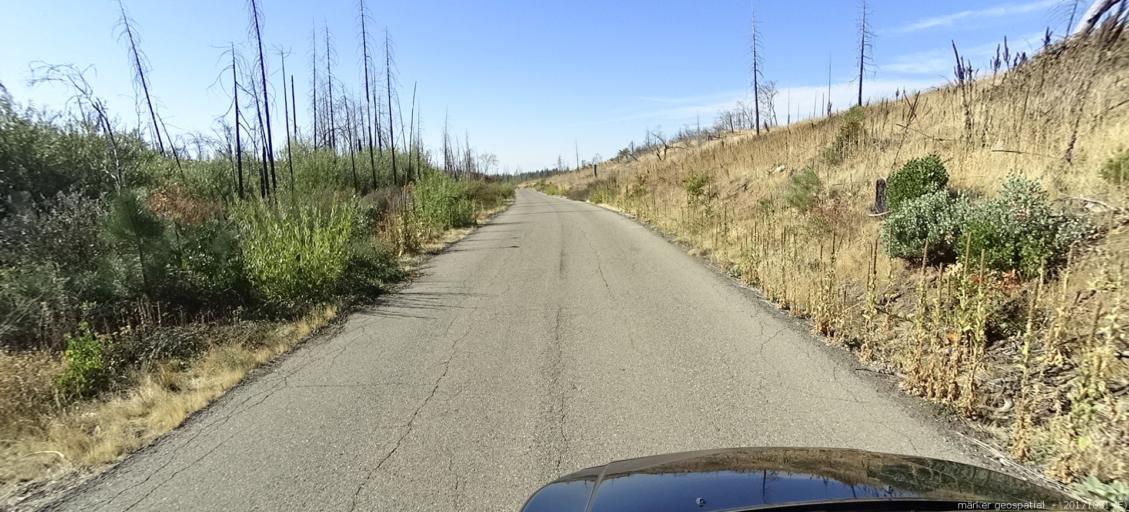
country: US
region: California
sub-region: Shasta County
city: Shingletown
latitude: 40.4545
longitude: -121.7964
